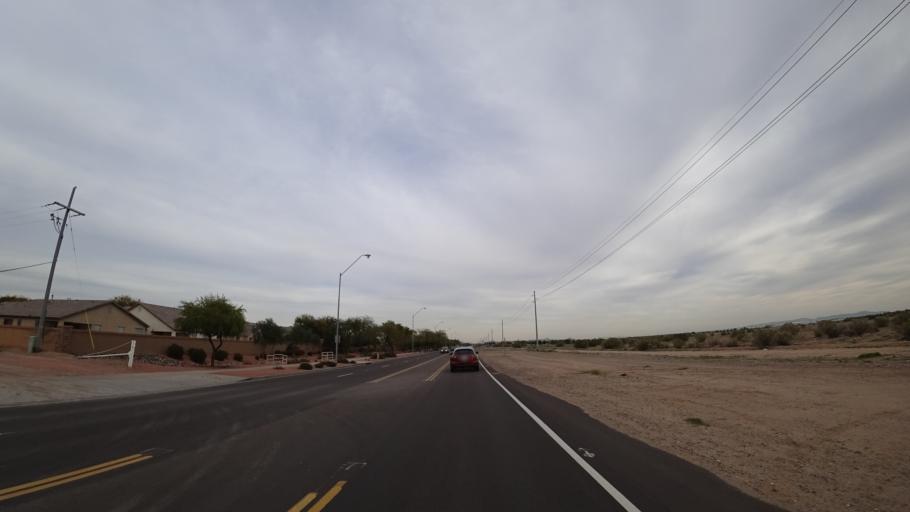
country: US
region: Arizona
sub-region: Maricopa County
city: Surprise
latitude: 33.6092
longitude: -112.3682
